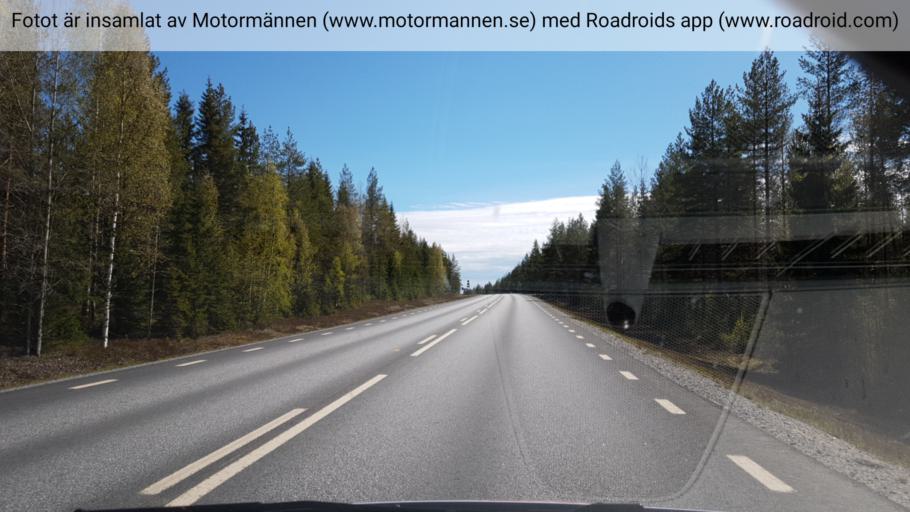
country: SE
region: Vaesterbotten
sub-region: Vannas Kommun
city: Vannasby
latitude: 64.0677
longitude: 19.9918
